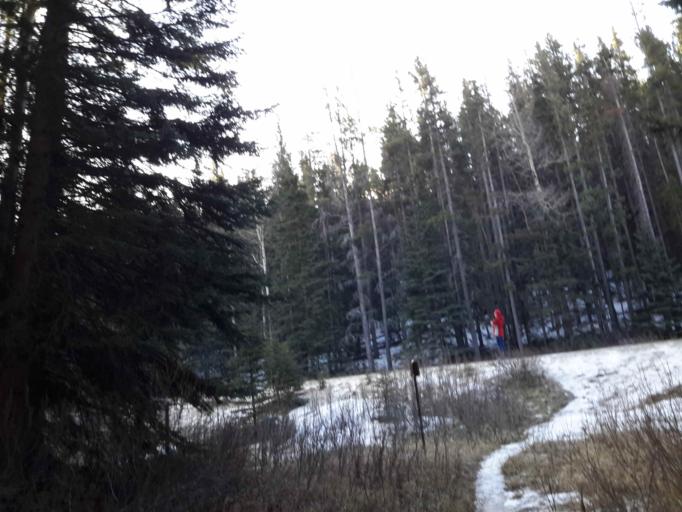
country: CA
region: Alberta
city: Banff
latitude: 51.2016
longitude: -115.5309
